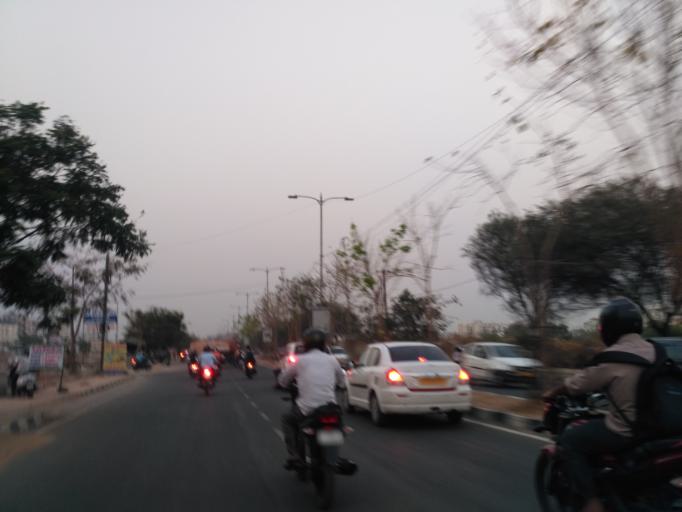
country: IN
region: Telangana
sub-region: Rangareddi
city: Kukatpalli
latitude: 17.4463
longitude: 78.3947
